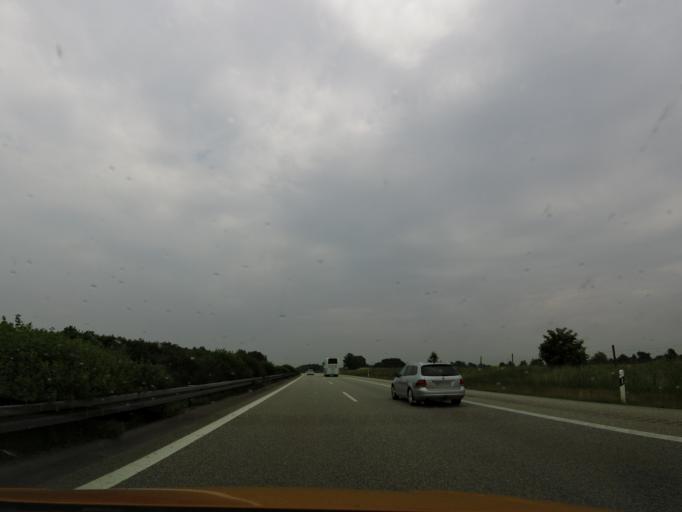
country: DE
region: Mecklenburg-Vorpommern
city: Rehna
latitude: 53.8182
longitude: 11.1097
